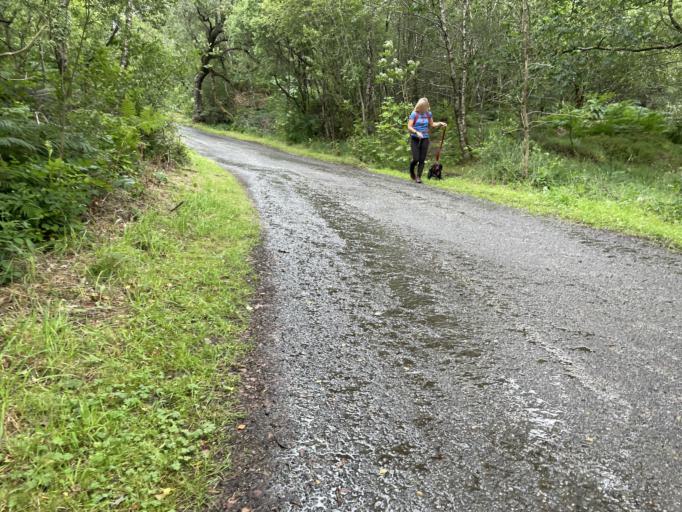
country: GB
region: Scotland
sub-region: Dumfries and Galloway
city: Newton Stewart
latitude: 55.0917
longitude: -4.4861
